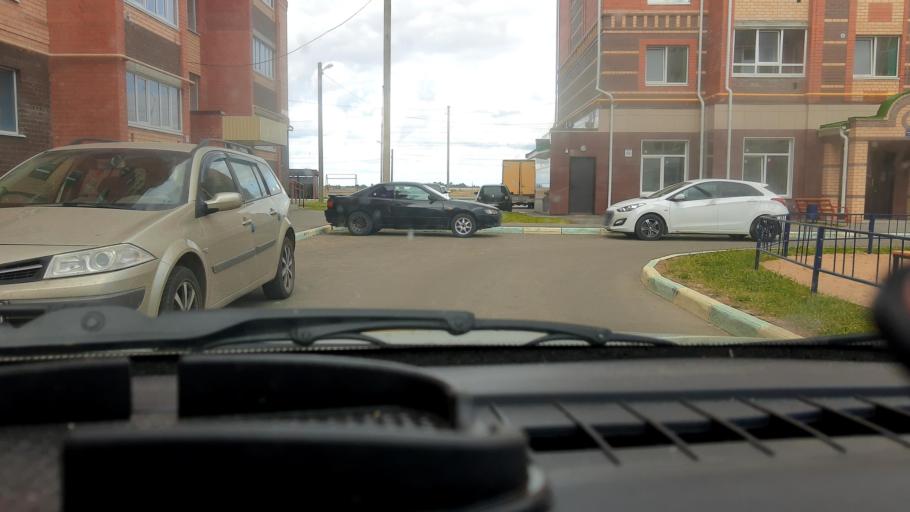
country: RU
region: Mariy-El
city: Medvedevo
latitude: 56.6382
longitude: 47.7965
